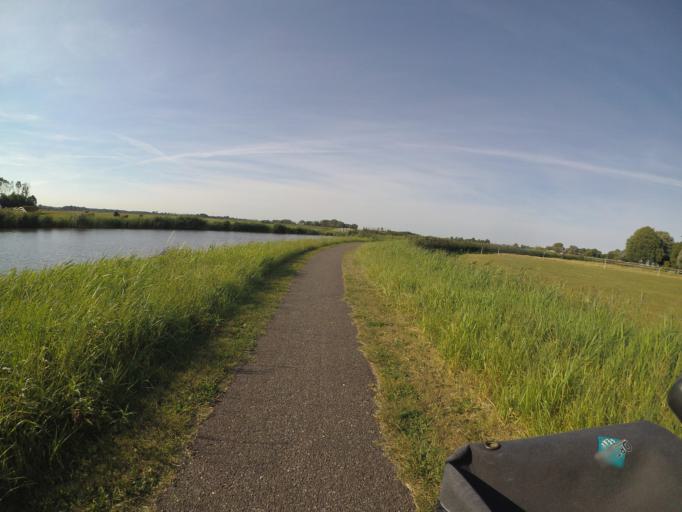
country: NL
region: Friesland
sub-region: Gemeente Dantumadiel
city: Rinsumageast
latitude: 53.3181
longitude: 5.9494
